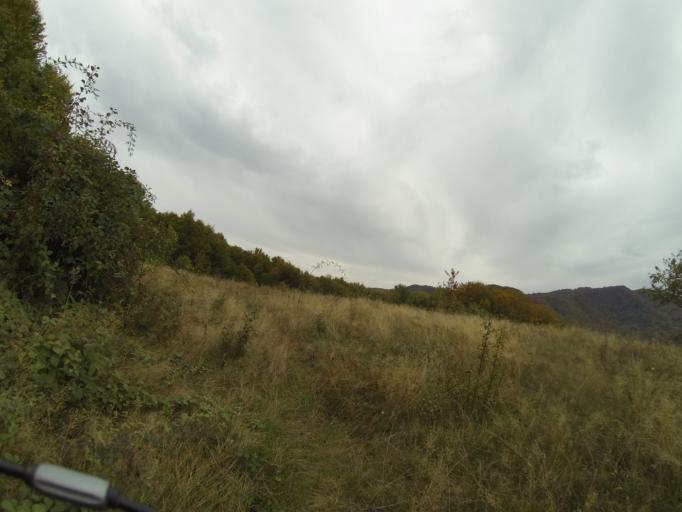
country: RO
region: Gorj
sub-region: Comuna Tismana
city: Sohodol
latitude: 45.0935
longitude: 22.8870
